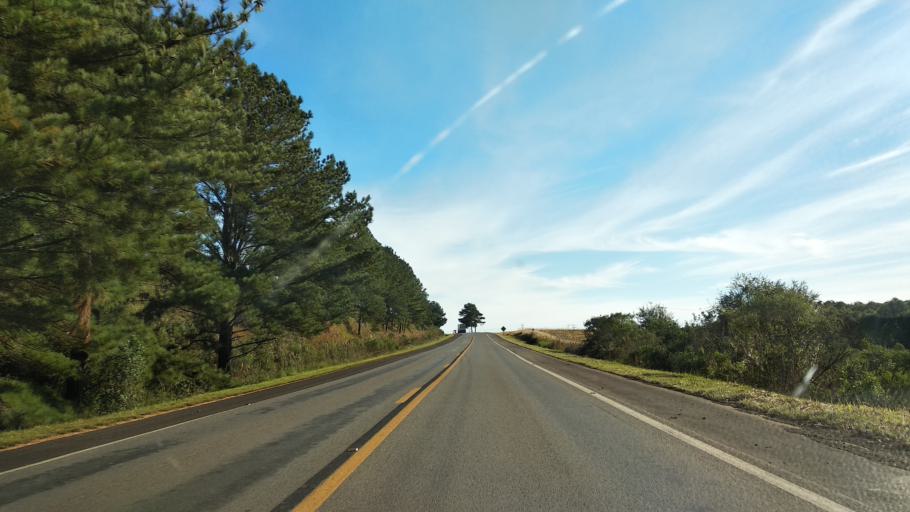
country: BR
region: Santa Catarina
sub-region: Celso Ramos
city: Celso Ramos
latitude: -27.5319
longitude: -51.3948
